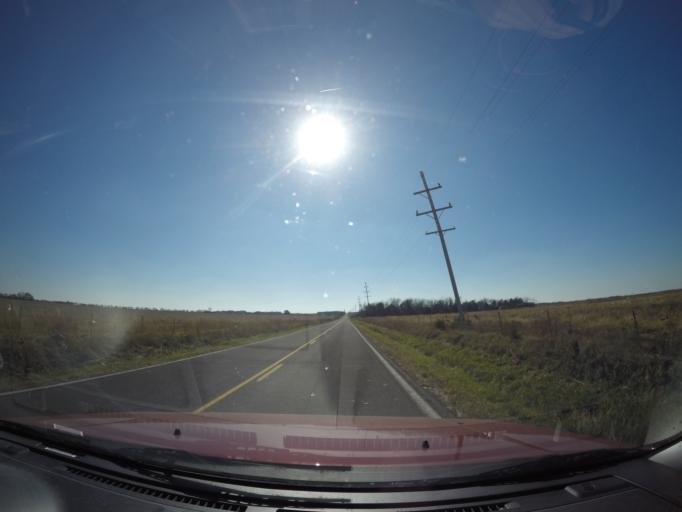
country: US
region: Kansas
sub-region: Morris County
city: Council Grove
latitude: 38.8685
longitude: -96.5941
